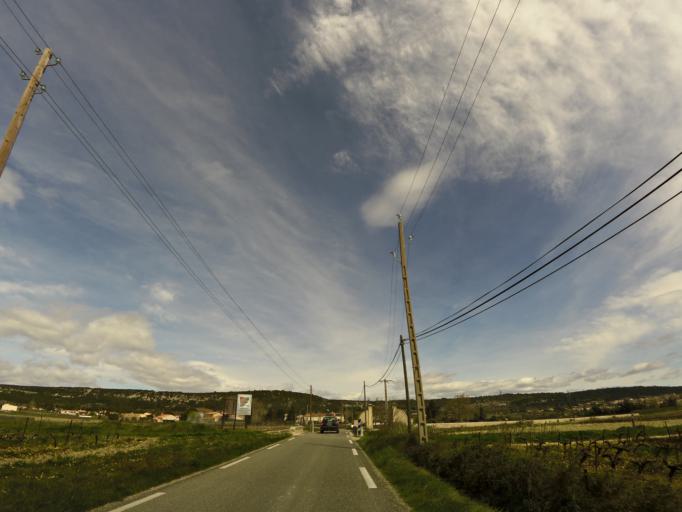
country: FR
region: Languedoc-Roussillon
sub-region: Departement du Gard
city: Clarensac
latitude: 43.8193
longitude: 4.2036
